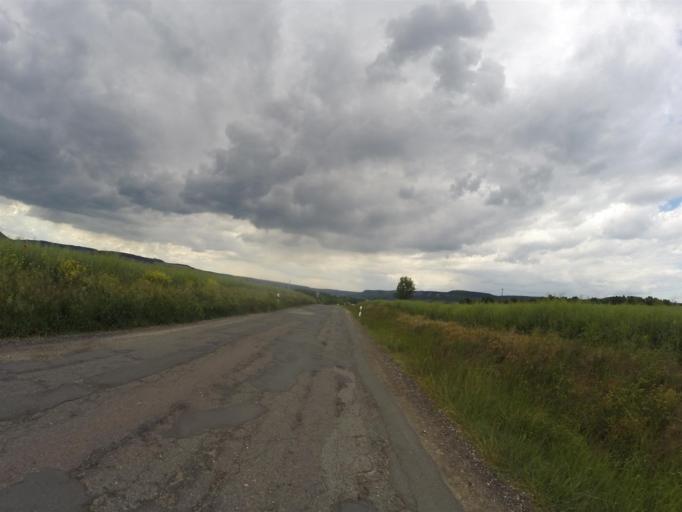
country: DE
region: Thuringia
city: Zollnitz
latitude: 50.8631
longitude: 11.6263
